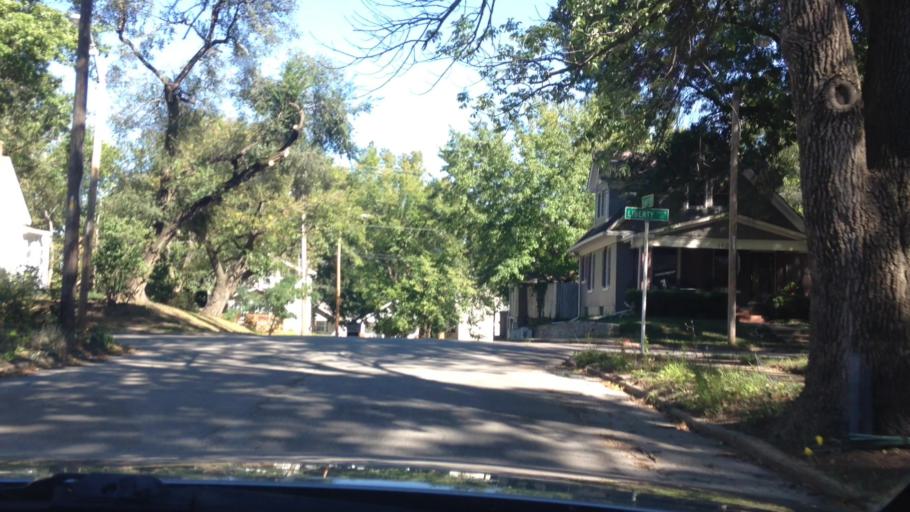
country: US
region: Kansas
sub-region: Johnson County
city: Westwood
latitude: 39.0445
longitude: -94.6037
